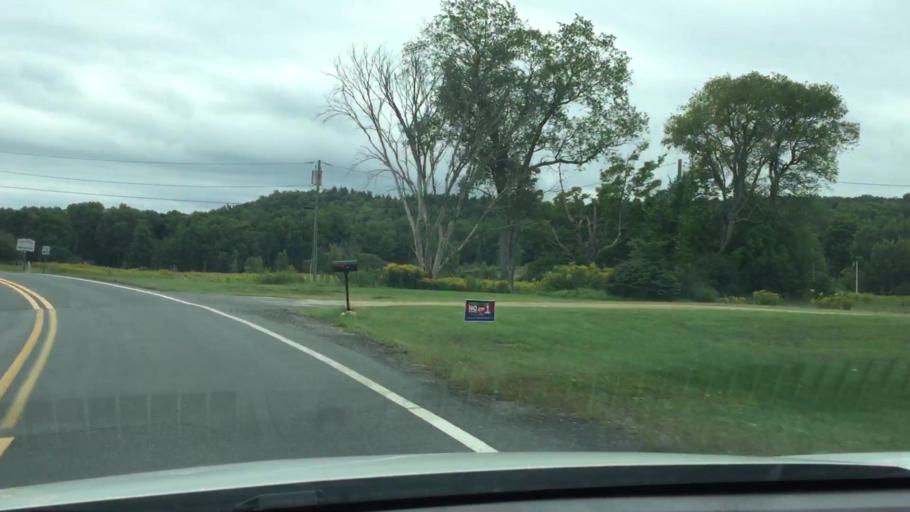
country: US
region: Massachusetts
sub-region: Berkshire County
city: Hinsdale
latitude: 42.3911
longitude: -73.1256
